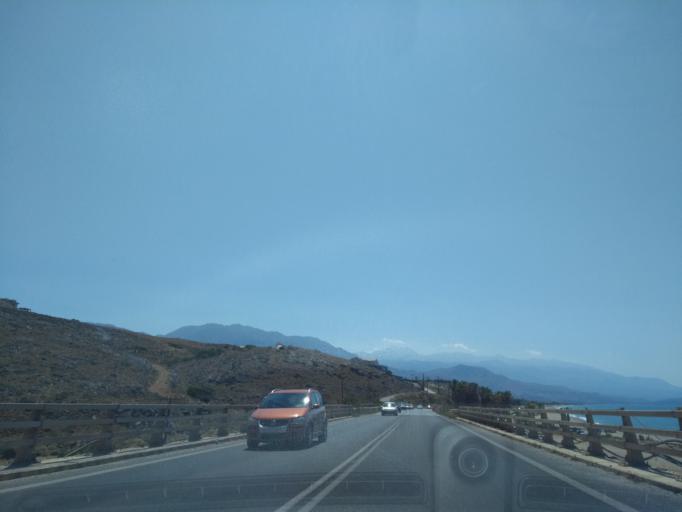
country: GR
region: Crete
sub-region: Nomos Rethymnis
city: Atsipopoulon
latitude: 35.3513
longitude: 24.3586
